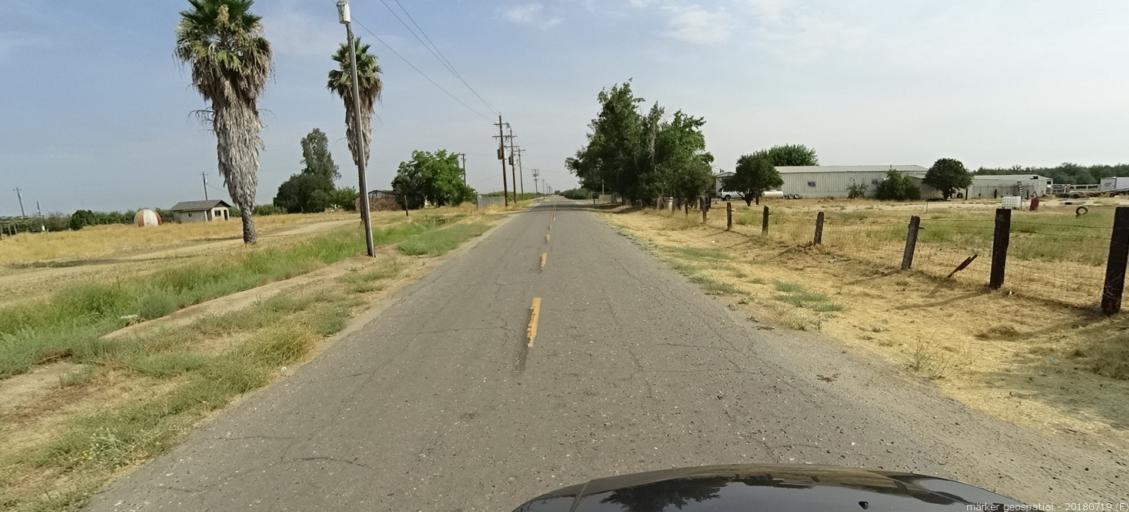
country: US
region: California
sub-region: Madera County
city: Fairmead
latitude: 37.1045
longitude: -120.2113
